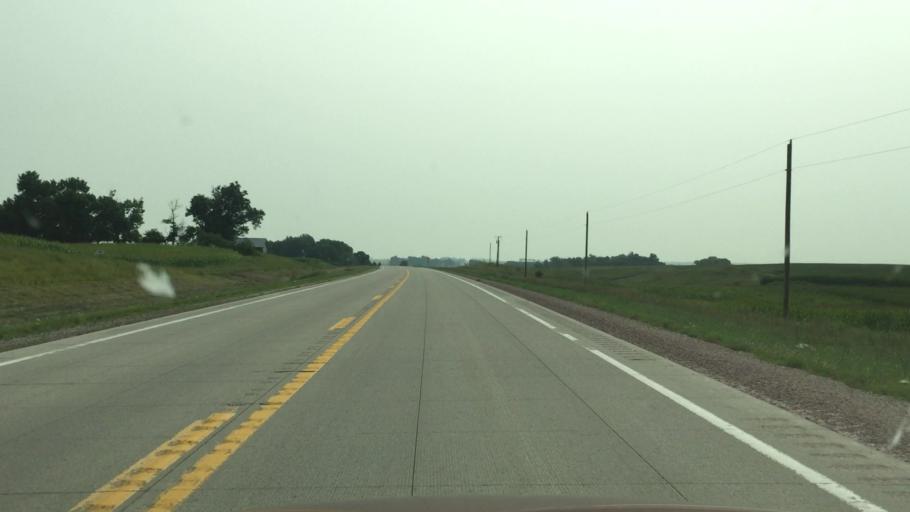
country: US
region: Iowa
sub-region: Osceola County
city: Sibley
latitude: 43.4329
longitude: -95.6262
